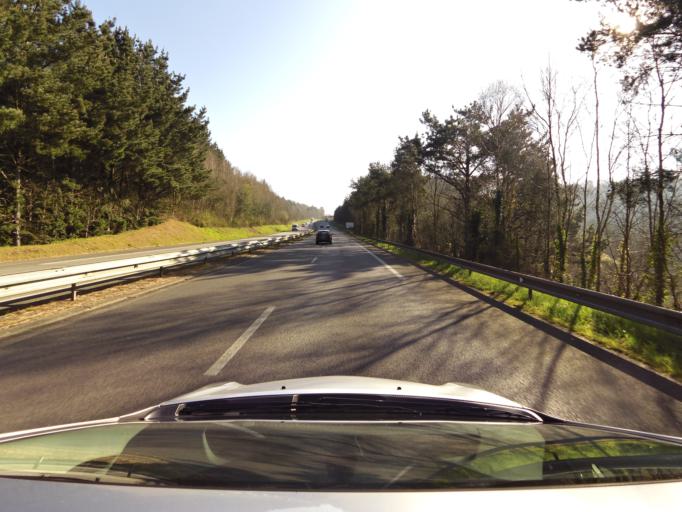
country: FR
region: Brittany
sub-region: Departement du Morbihan
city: Guenin
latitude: 47.8938
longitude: -2.9668
